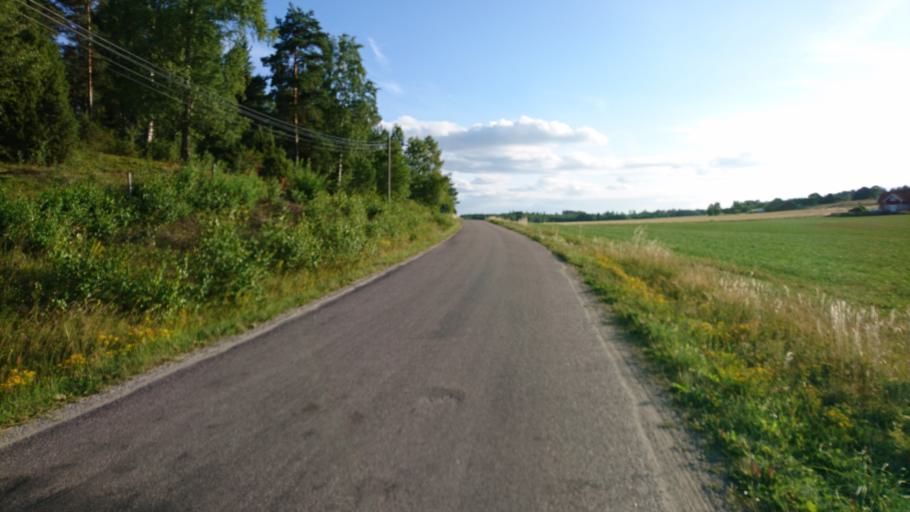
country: SE
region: Soedermanland
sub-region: Strangnas Kommun
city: Stallarholmen
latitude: 59.4034
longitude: 17.2823
